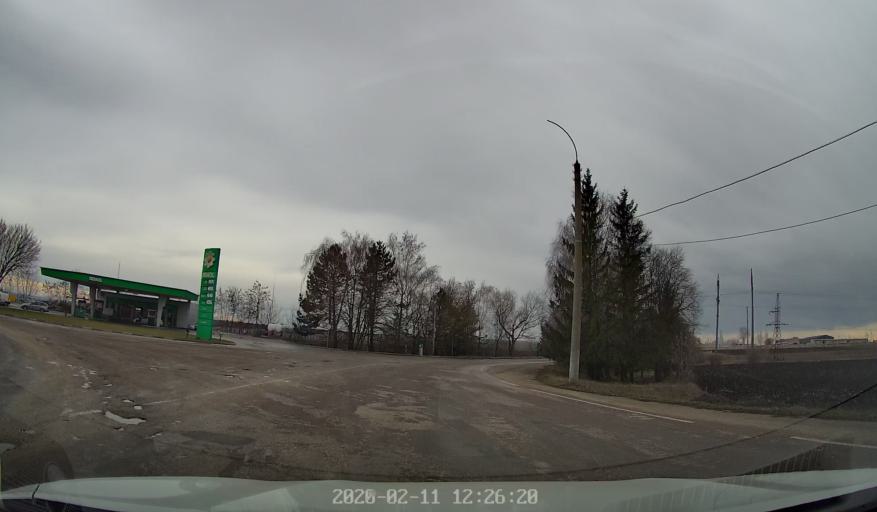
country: MD
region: Raionul Edinet
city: Edinet
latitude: 48.1589
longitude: 27.3296
